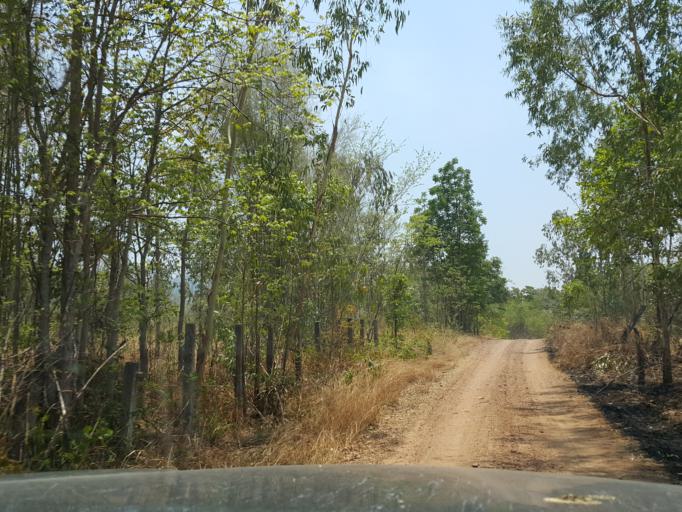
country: TH
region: Lampang
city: Thoen
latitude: 17.6398
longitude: 99.2766
